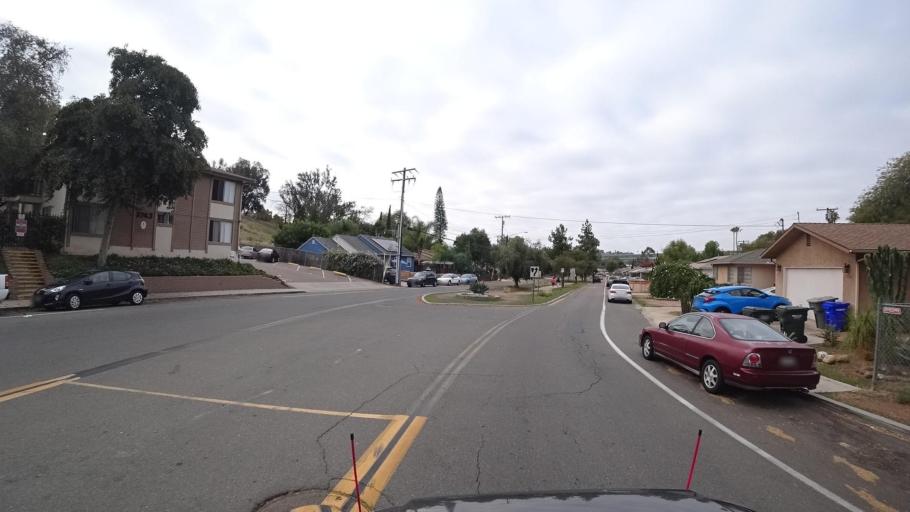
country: US
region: California
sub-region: San Diego County
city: Spring Valley
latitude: 32.7509
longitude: -117.0125
